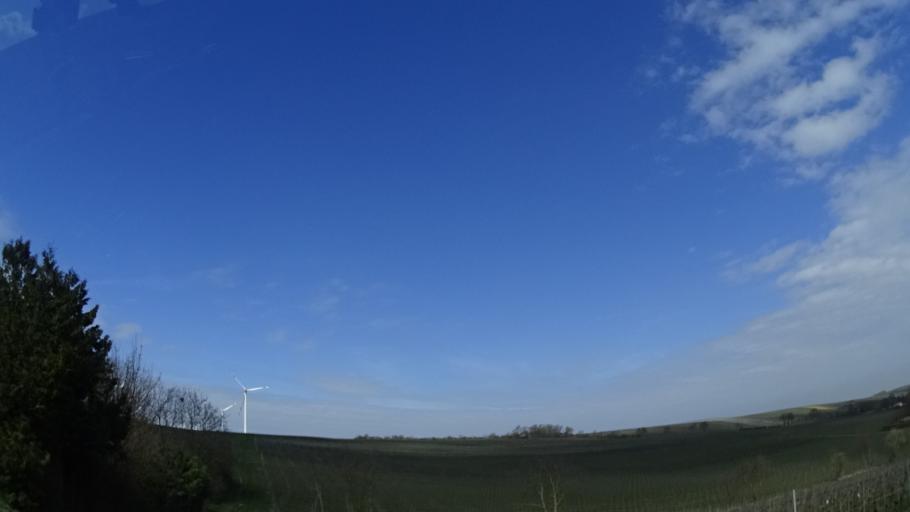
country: DE
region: Rheinland-Pfalz
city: Lonsheim
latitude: 49.7590
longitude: 8.0745
